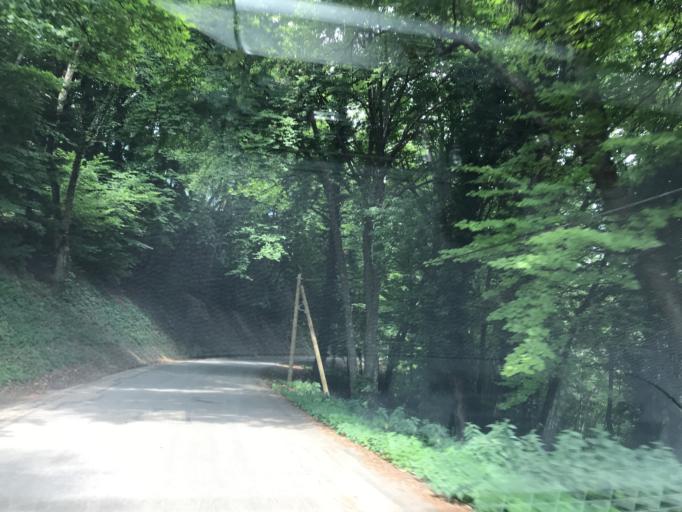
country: FR
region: Rhone-Alpes
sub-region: Departement de l'Isere
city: Barraux
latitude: 45.4526
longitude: 5.9640
